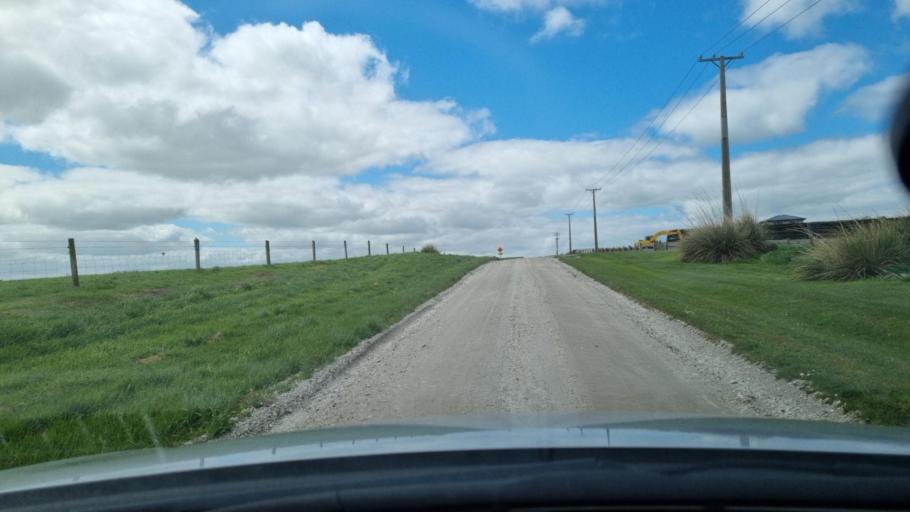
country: NZ
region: Southland
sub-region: Invercargill City
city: Invercargill
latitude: -46.4506
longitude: 168.4152
